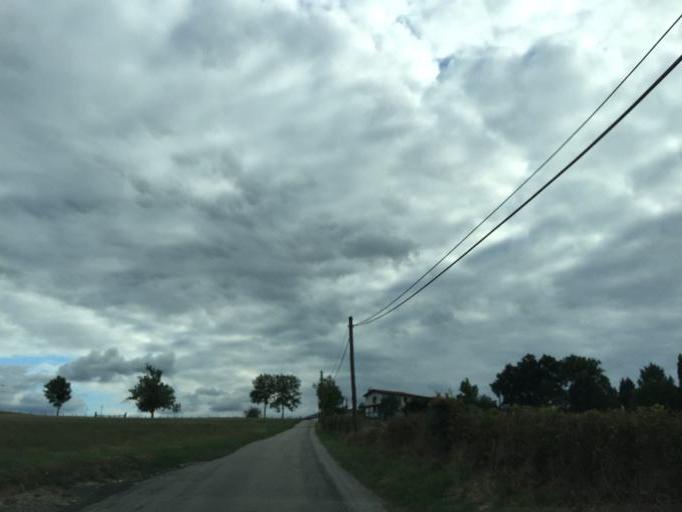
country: FR
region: Rhone-Alpes
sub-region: Departement de la Loire
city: Saint-Chamond
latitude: 45.4866
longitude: 4.4954
